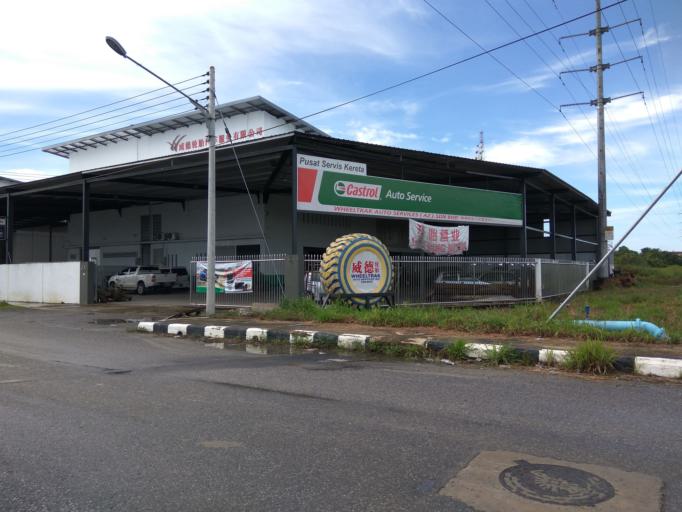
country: MY
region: Sarawak
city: Sibu
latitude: 2.2696
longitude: 111.8675
